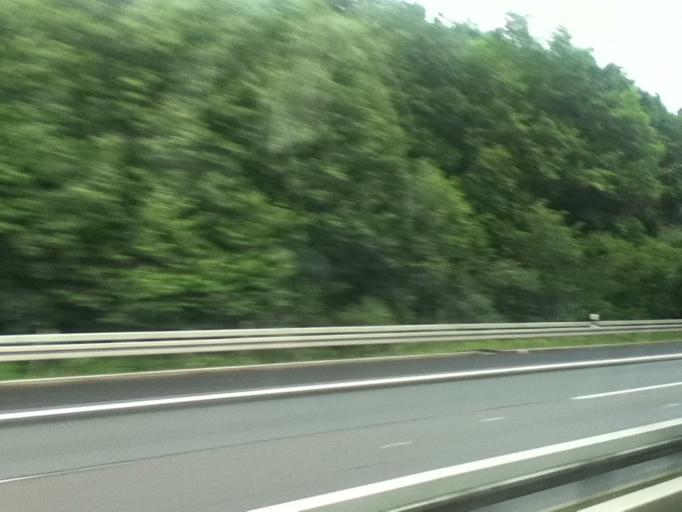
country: DE
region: Hesse
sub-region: Regierungsbezirk Giessen
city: Asslar
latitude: 50.6025
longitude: 8.4733
